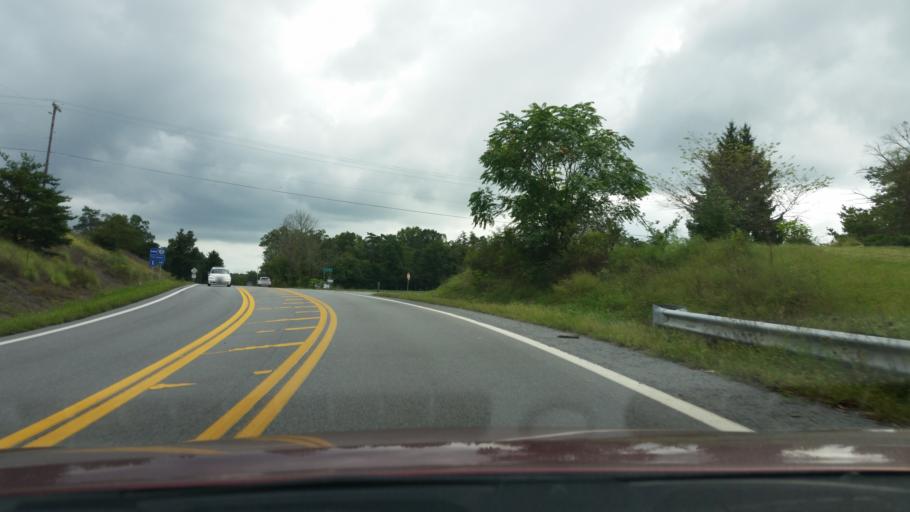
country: US
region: Maryland
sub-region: Washington County
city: Hancock
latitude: 39.5950
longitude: -78.0674
